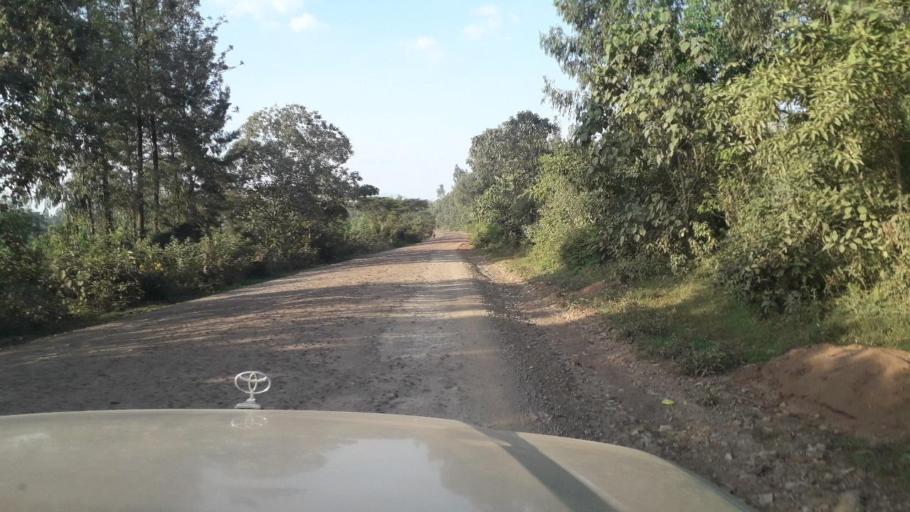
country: ET
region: Oromiya
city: Jima
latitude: 7.5770
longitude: 36.8579
